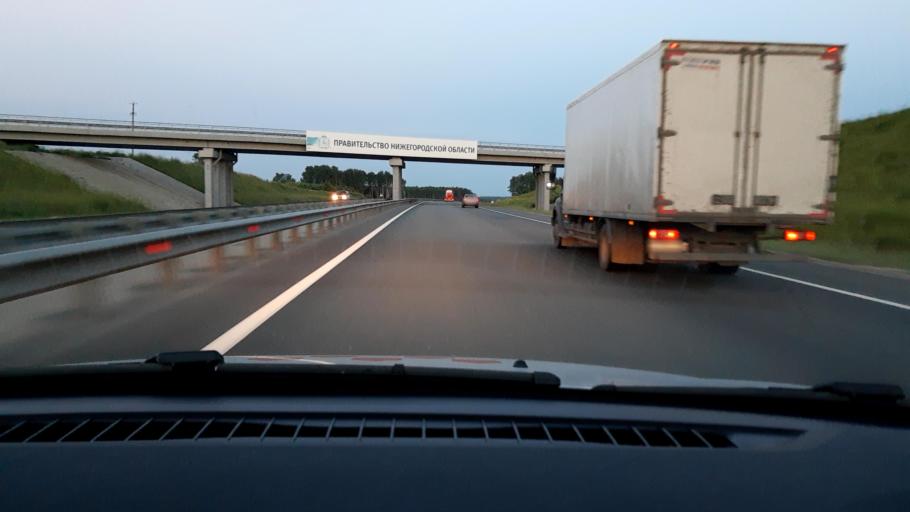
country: RU
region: Nizjnij Novgorod
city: Kstovo
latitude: 56.0929
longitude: 44.0785
